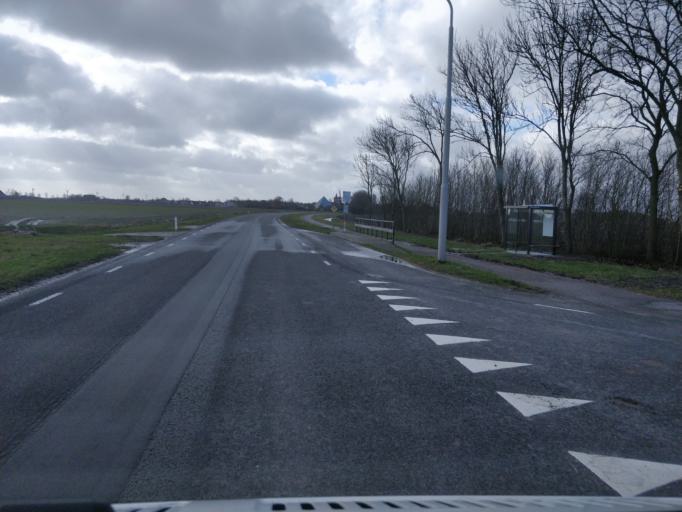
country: NL
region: Friesland
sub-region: Gemeente Franekeradeel
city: Sexbierum
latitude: 53.2267
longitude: 5.4957
